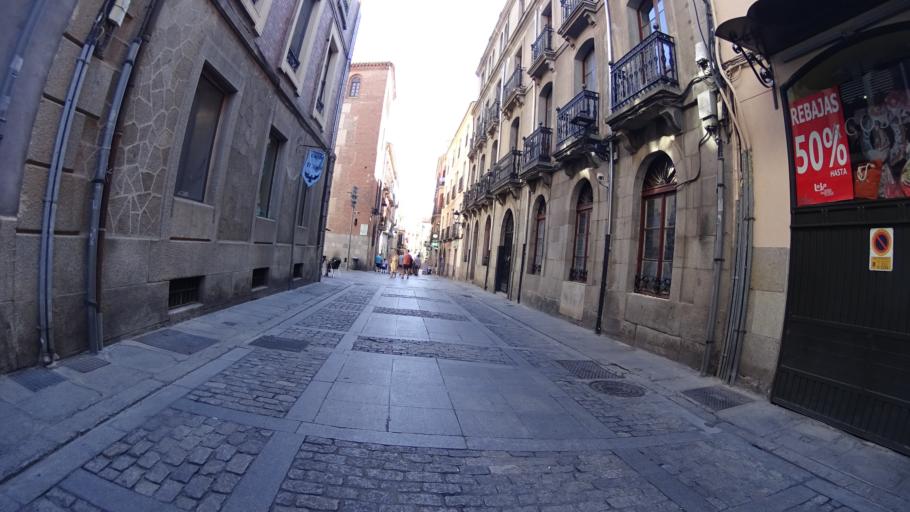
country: ES
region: Castille and Leon
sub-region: Provincia de Avila
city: Avila
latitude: 40.6561
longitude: -4.6983
